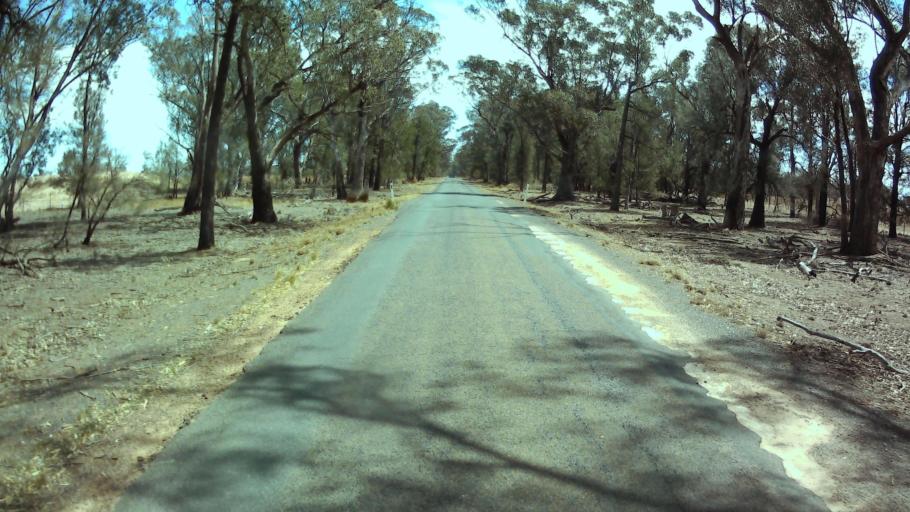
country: AU
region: New South Wales
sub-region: Weddin
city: Grenfell
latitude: -33.6523
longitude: 148.1956
